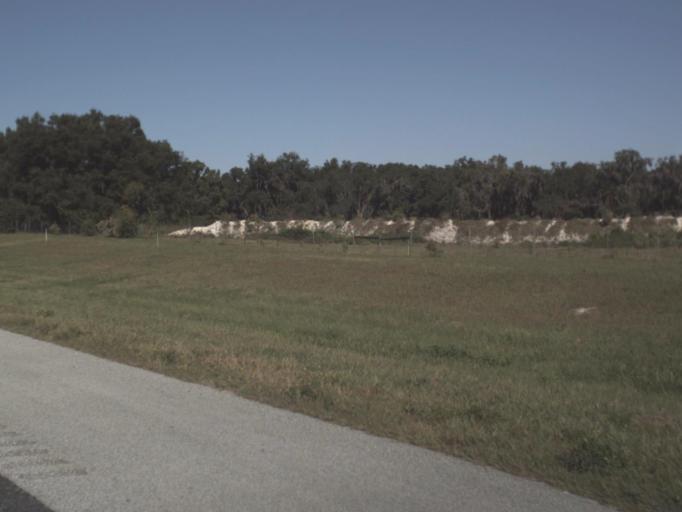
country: US
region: Florida
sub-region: Sumter County
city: Wildwood
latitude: 28.8019
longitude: -82.0013
